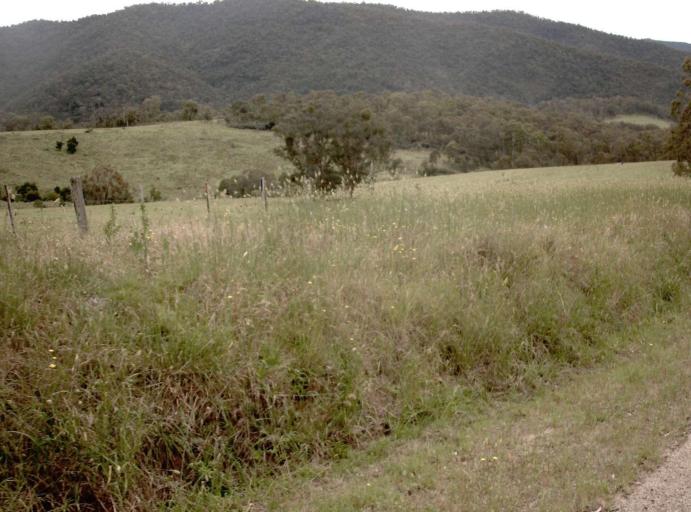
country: AU
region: Victoria
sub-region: East Gippsland
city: Bairnsdale
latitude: -37.5598
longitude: 147.1951
